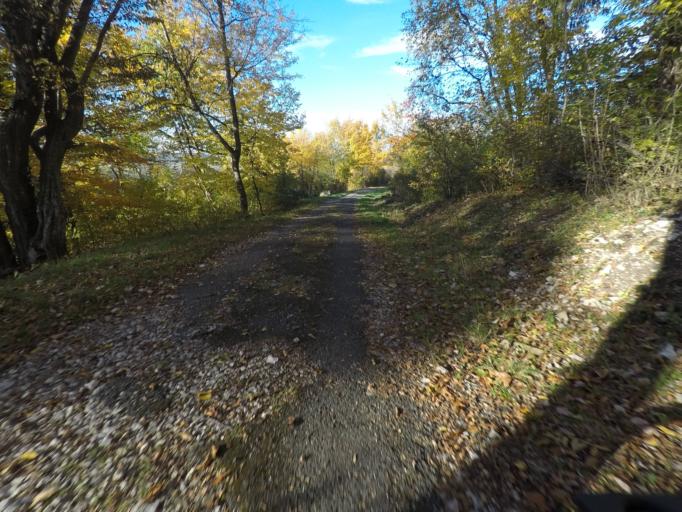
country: DE
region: Baden-Wuerttemberg
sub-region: Tuebingen Region
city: Pfullingen
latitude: 48.4427
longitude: 9.2153
